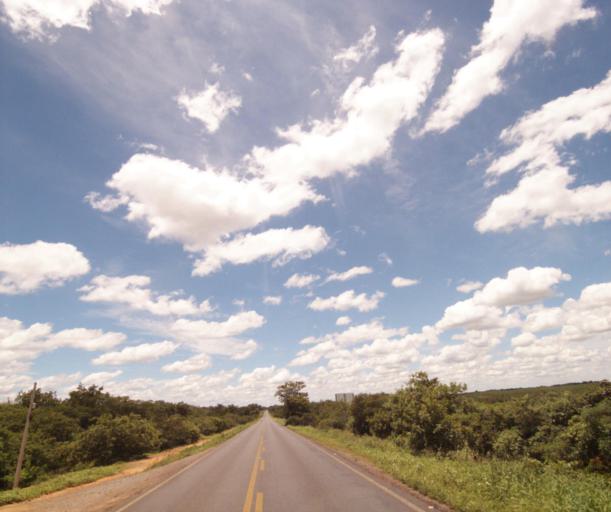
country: BR
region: Bahia
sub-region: Bom Jesus Da Lapa
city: Bom Jesus da Lapa
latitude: -13.2622
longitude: -43.5342
